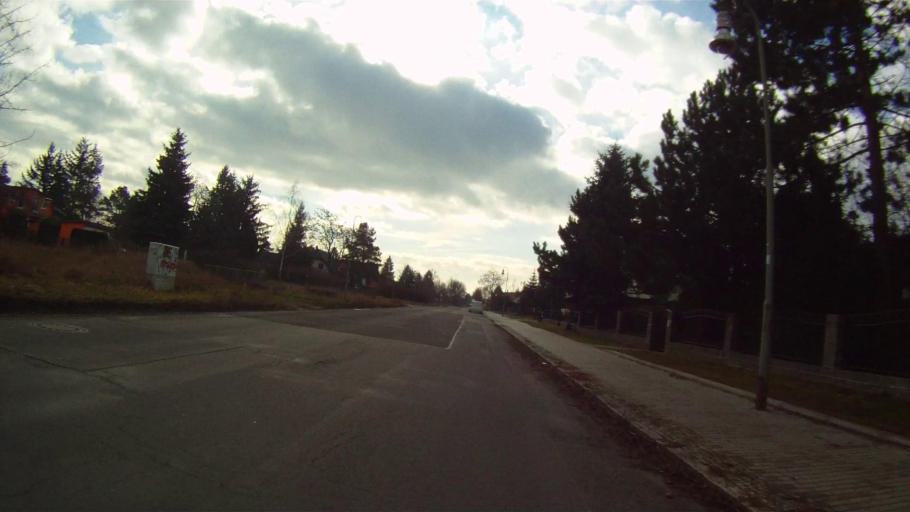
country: DE
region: Berlin
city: Biesdorf
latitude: 52.4960
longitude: 13.5552
